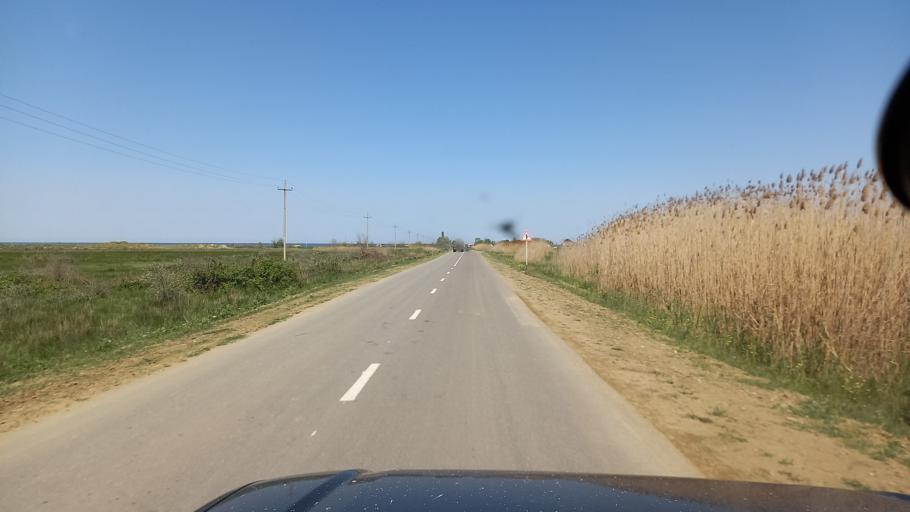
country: RU
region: Dagestan
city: Khazar
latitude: 41.9479
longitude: 48.3532
